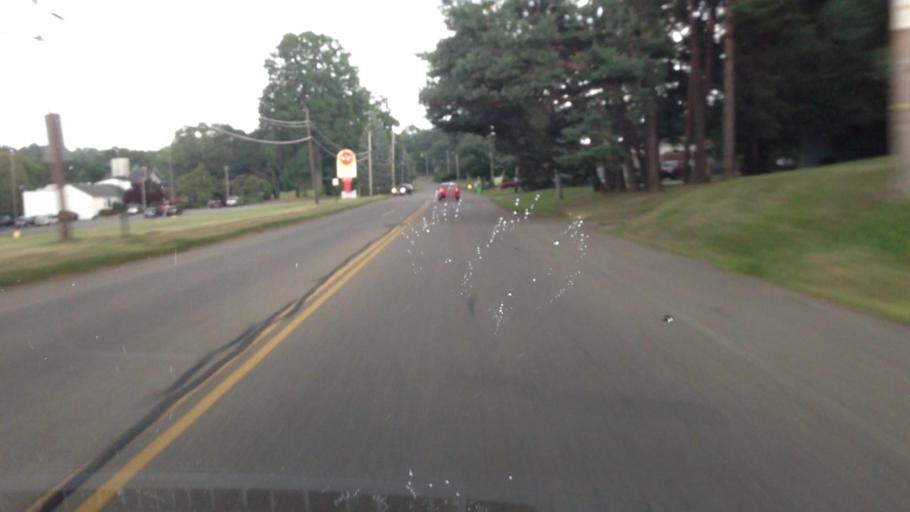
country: US
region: Ohio
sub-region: Summit County
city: Barberton
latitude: 41.0203
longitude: -81.5814
